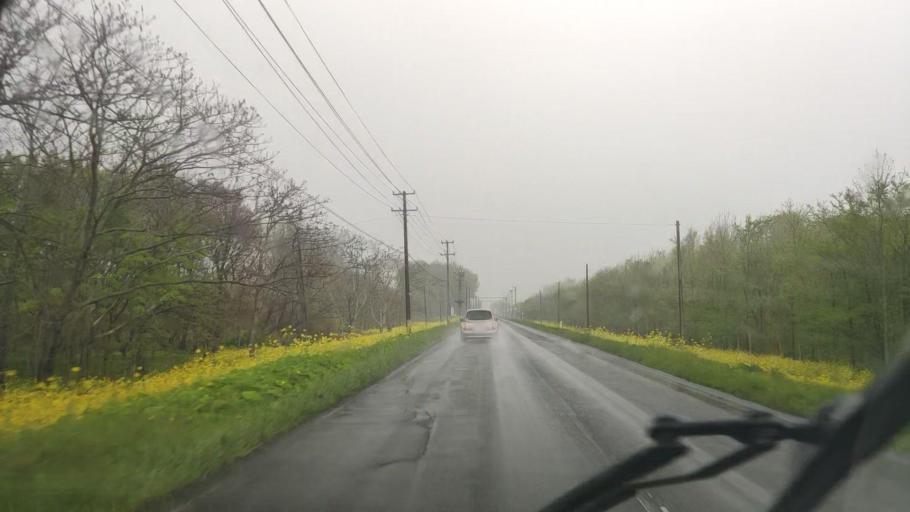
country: JP
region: Akita
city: Tenno
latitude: 39.9513
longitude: 139.9459
